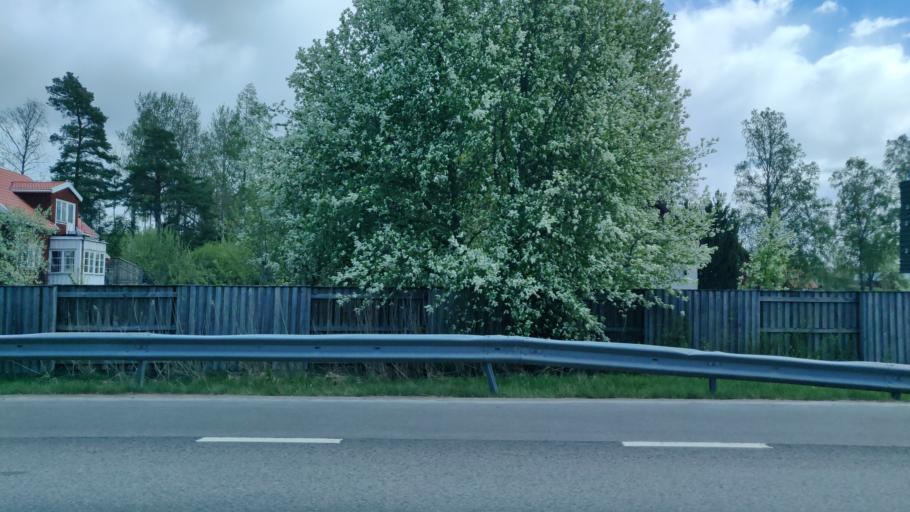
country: SE
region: Vaermland
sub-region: Karlstads Kommun
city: Molkom
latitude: 59.6008
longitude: 13.7374
